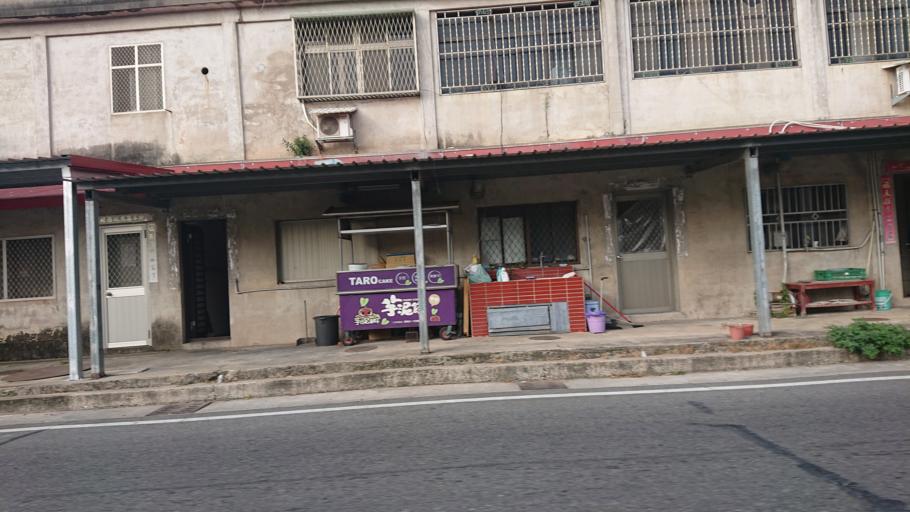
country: TW
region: Fukien
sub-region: Kinmen
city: Jincheng
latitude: 24.4776
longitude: 118.4280
